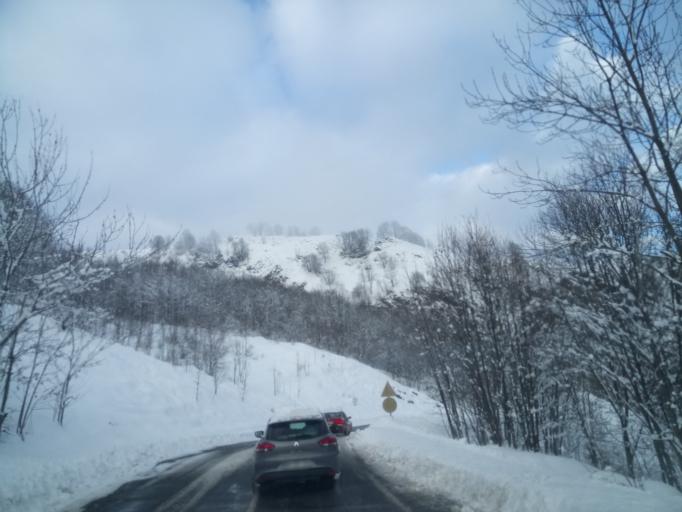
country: FR
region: Rhone-Alpes
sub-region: Departement de la Savoie
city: Saint-Jean-de-Maurienne
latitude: 45.2481
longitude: 6.2828
